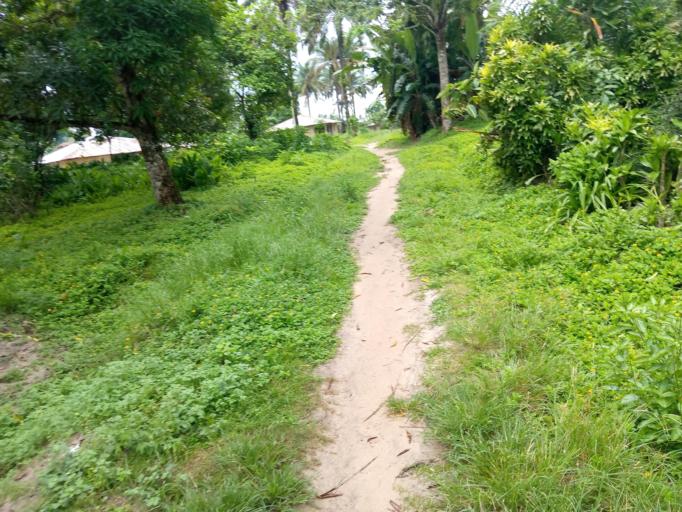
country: SL
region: Southern Province
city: Bonthe
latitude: 7.5333
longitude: -12.5047
